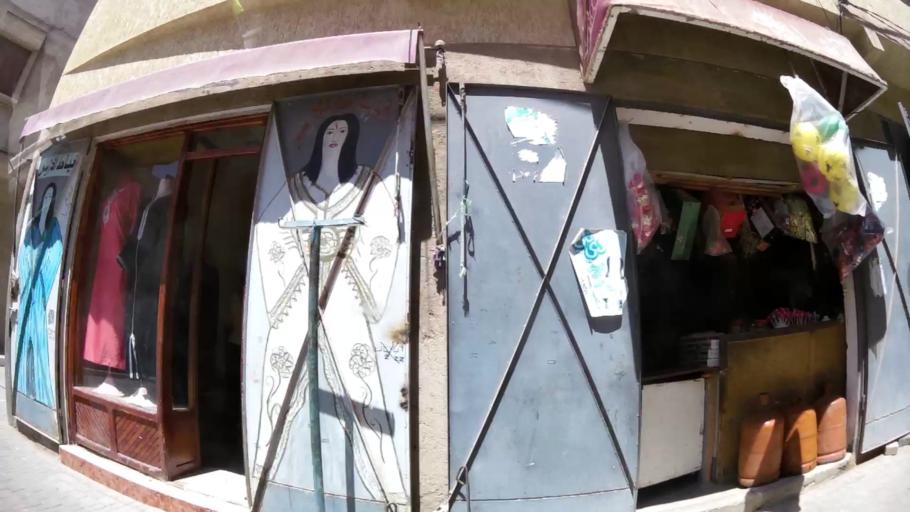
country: MA
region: Oriental
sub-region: Oujda-Angad
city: Oujda
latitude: 34.6810
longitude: -1.9554
